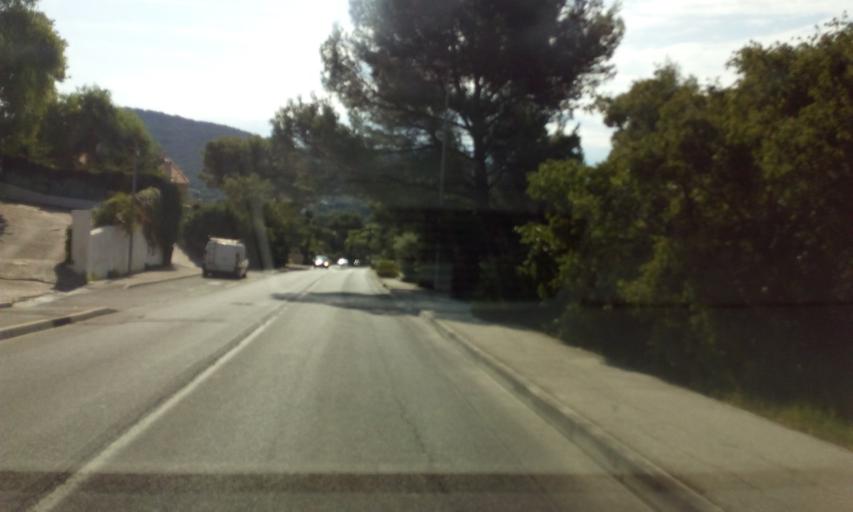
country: FR
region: Provence-Alpes-Cote d'Azur
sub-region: Departement du Var
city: Le Pradet
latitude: 43.0989
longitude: 6.0234
